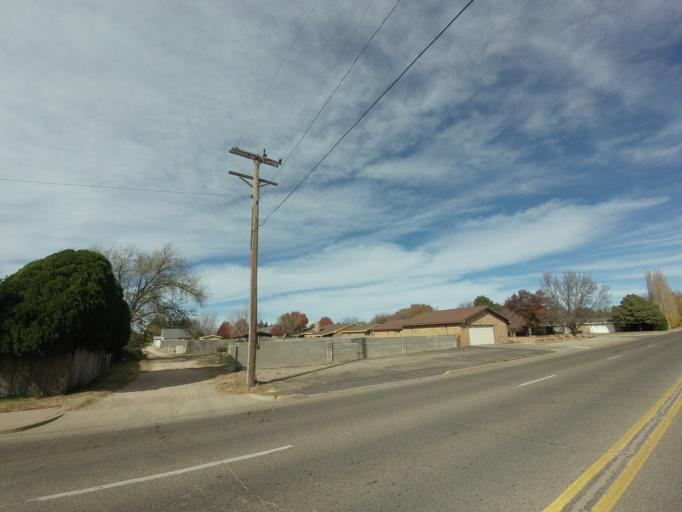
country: US
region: New Mexico
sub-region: Curry County
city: Clovis
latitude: 34.4169
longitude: -103.1788
